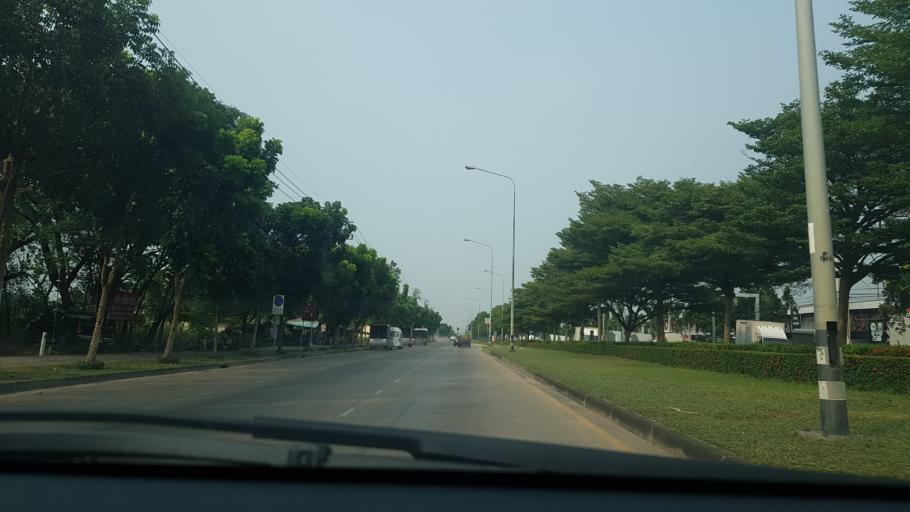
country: TH
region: Bangkok
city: Phasi Charoen
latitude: 13.7579
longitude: 100.3951
